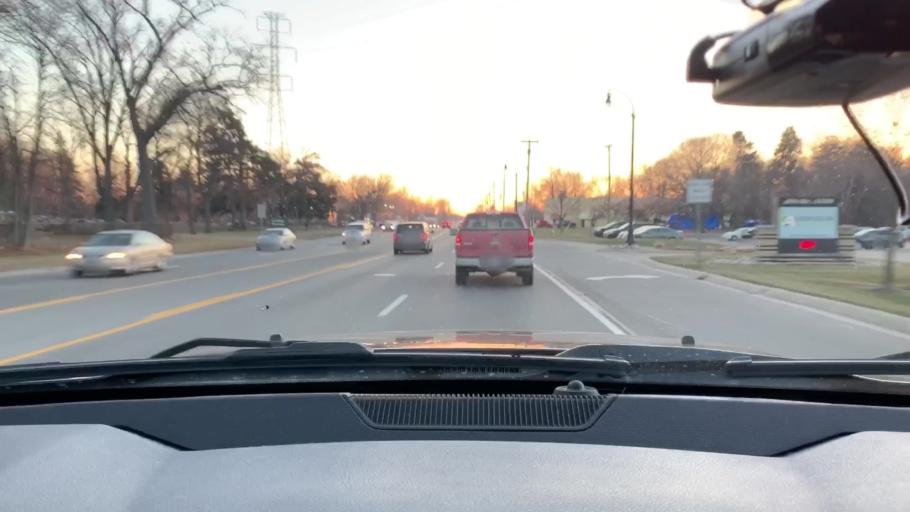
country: US
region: Michigan
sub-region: Wayne County
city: Woodhaven
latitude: 42.1326
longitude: -83.2702
